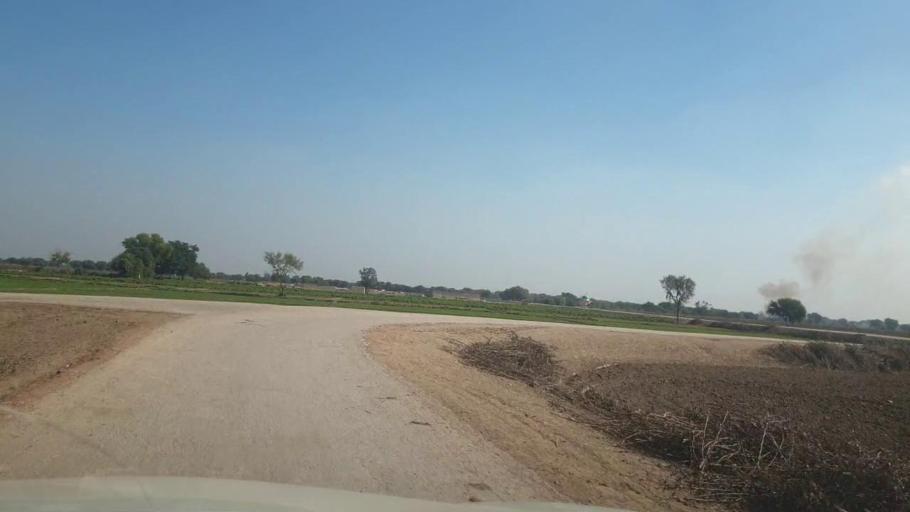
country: PK
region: Sindh
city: Bhan
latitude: 26.5798
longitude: 67.7004
